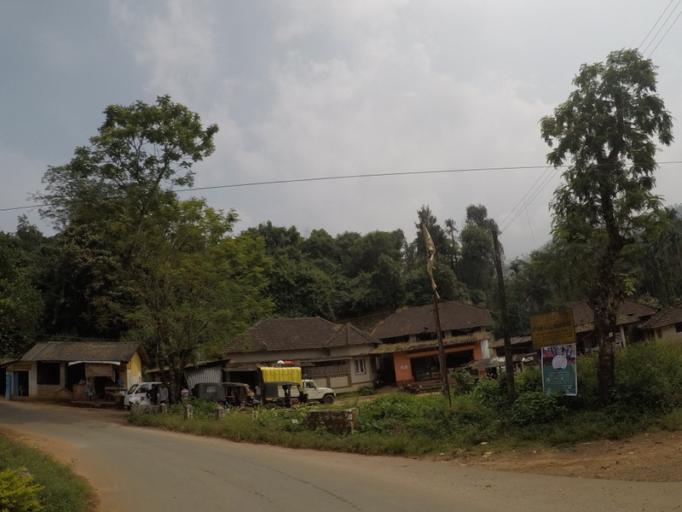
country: IN
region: Karnataka
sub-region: Chikmagalur
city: Mudigere
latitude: 13.1581
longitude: 75.4467
